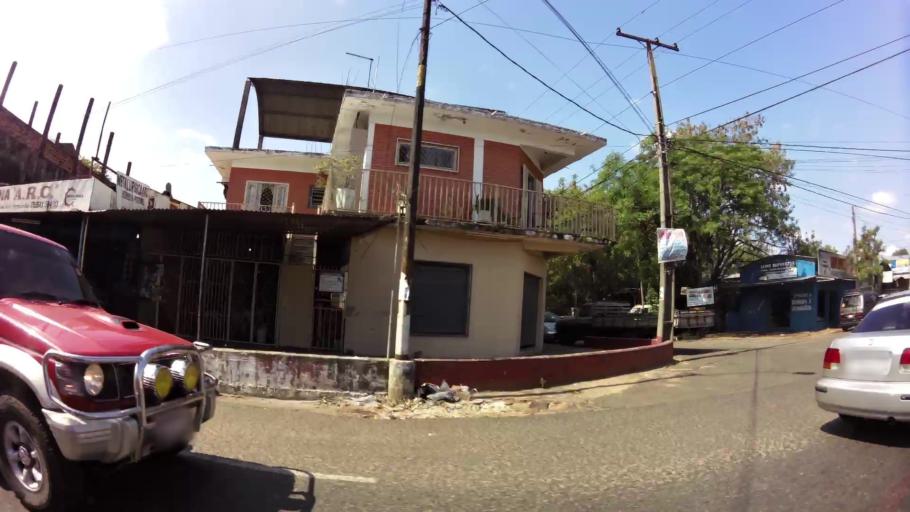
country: PY
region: Central
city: San Lorenzo
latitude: -25.3455
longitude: -57.5152
